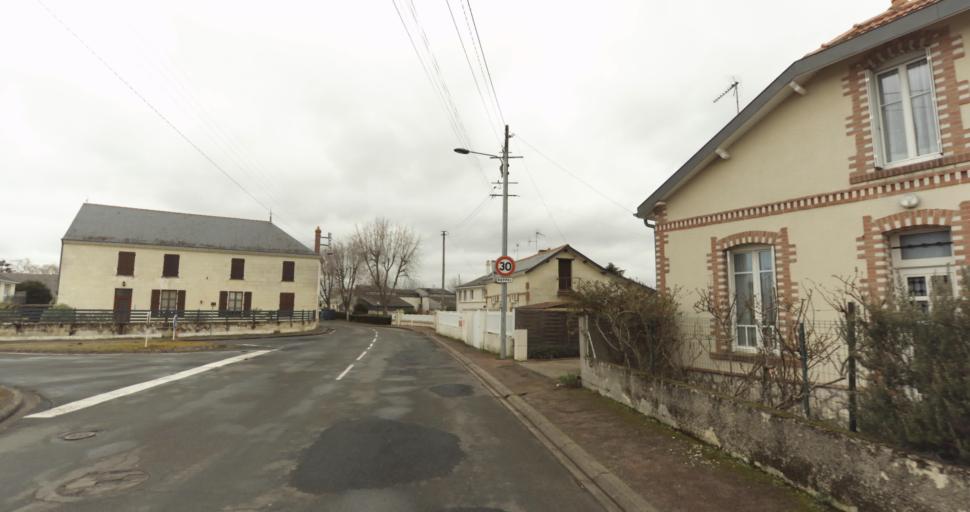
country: FR
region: Pays de la Loire
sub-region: Departement de Maine-et-Loire
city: Distre
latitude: 47.2402
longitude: -0.0937
